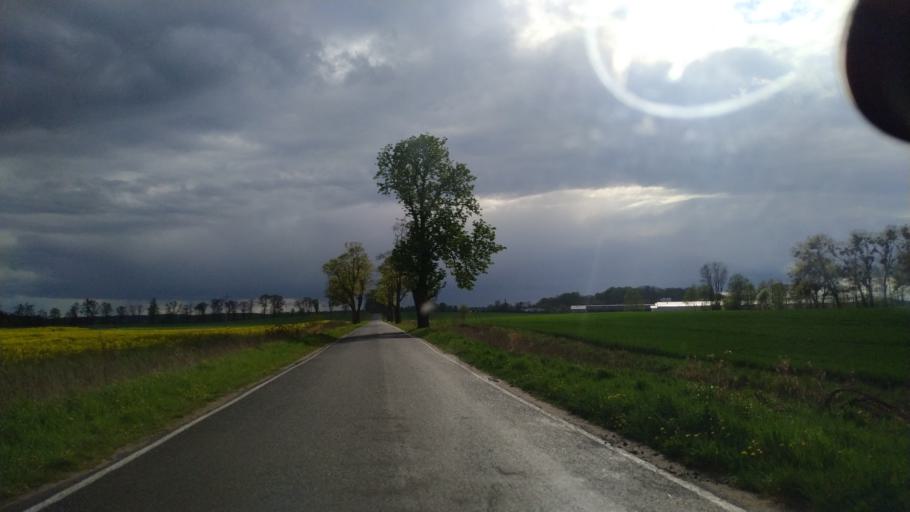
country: PL
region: Pomeranian Voivodeship
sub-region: Powiat starogardzki
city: Smetowo Graniczne
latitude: 53.7231
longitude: 18.6233
